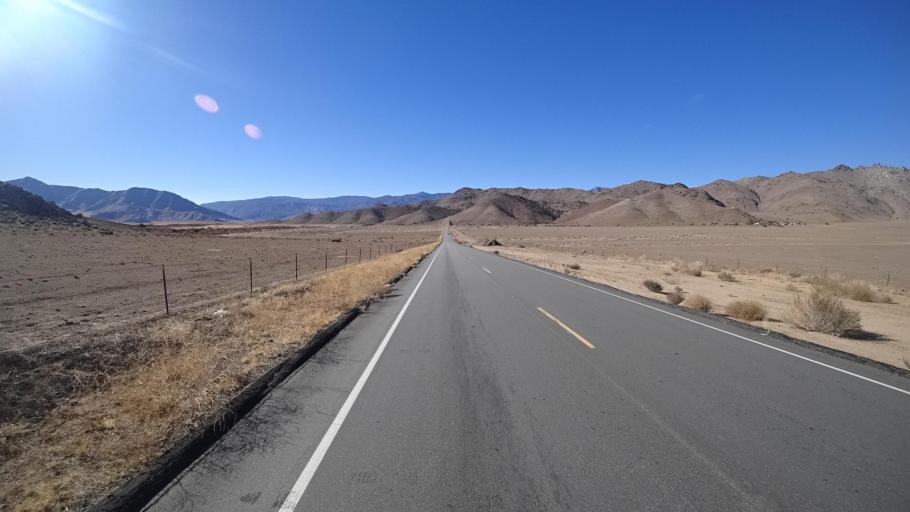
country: US
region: California
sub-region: Kern County
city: Weldon
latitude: 35.6785
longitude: -118.3626
